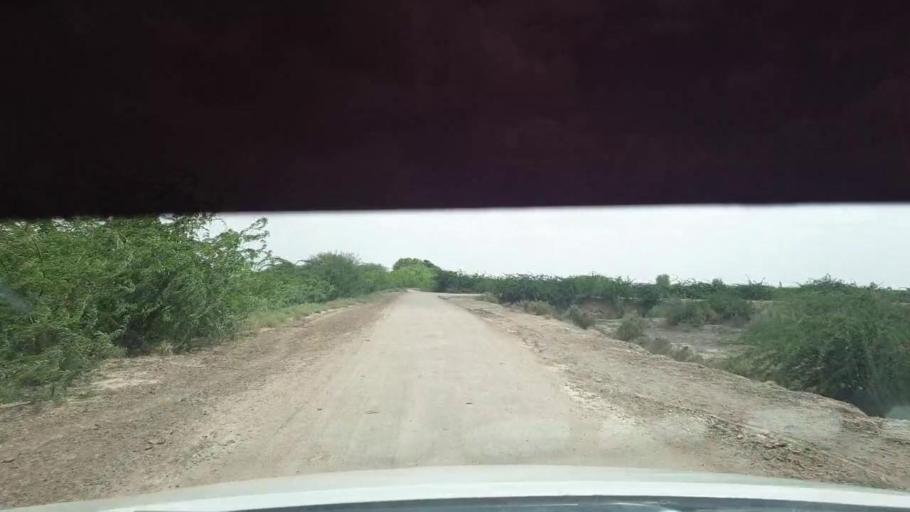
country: PK
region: Sindh
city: Kadhan
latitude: 24.5258
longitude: 69.0865
